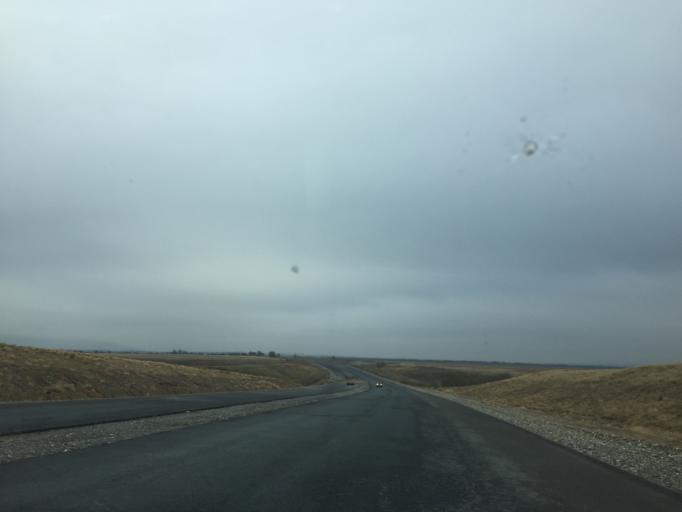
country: KZ
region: Ongtustik Qazaqstan
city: Kokterek
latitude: 42.5429
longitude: 70.1904
